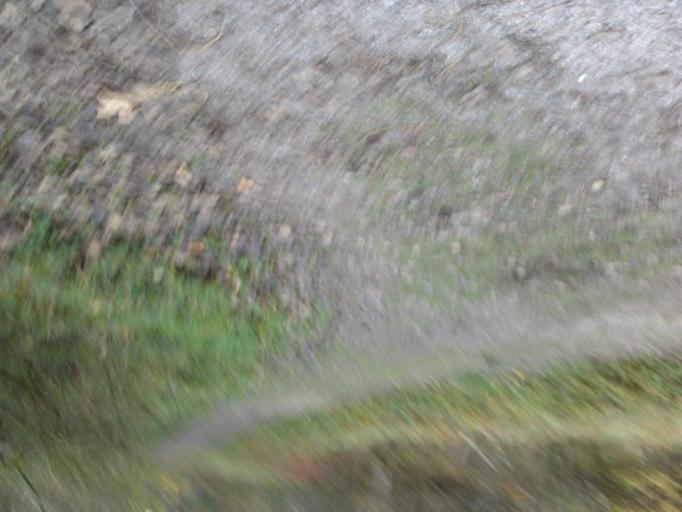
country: NL
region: South Holland
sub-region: Gemeente Noordwijkerhout
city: Noordwijkerhout
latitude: 52.2719
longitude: 4.4639
